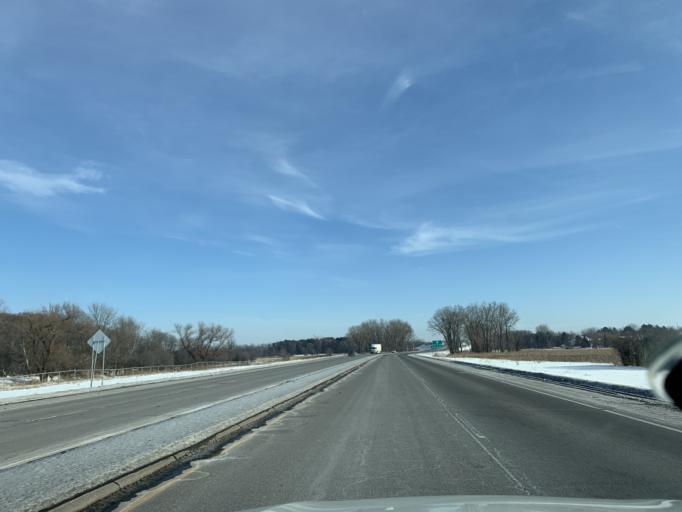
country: US
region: Minnesota
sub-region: Washington County
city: Forest Lake
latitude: 45.2898
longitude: -92.9972
